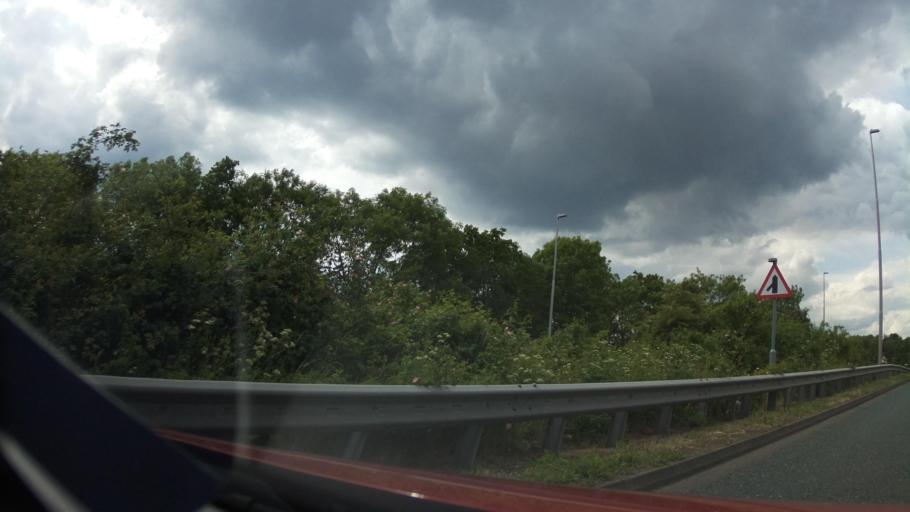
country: GB
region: England
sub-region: Sunderland
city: Washington
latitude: 54.9020
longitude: -1.5501
